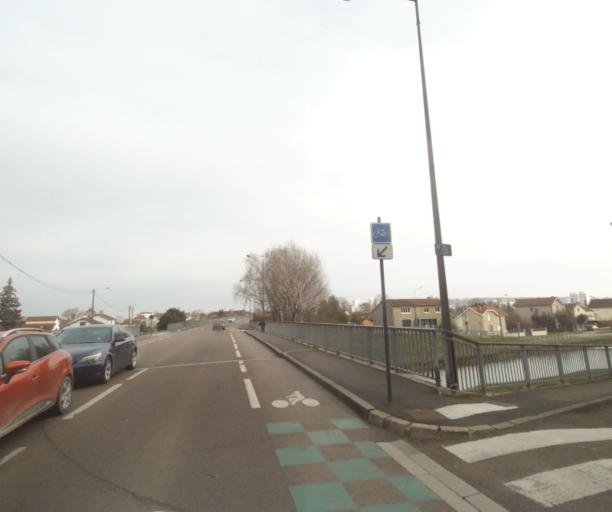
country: FR
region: Champagne-Ardenne
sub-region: Departement de la Haute-Marne
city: Saint-Dizier
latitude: 48.6380
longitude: 4.9583
